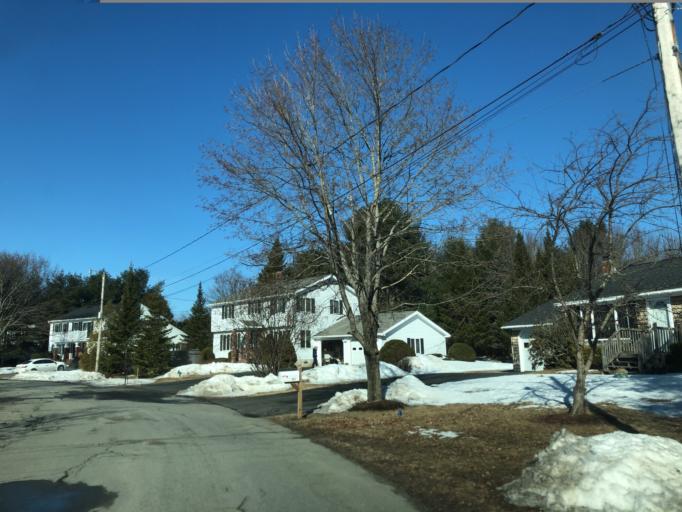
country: US
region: Maine
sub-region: Penobscot County
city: Brewer
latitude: 44.8210
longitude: -68.7458
